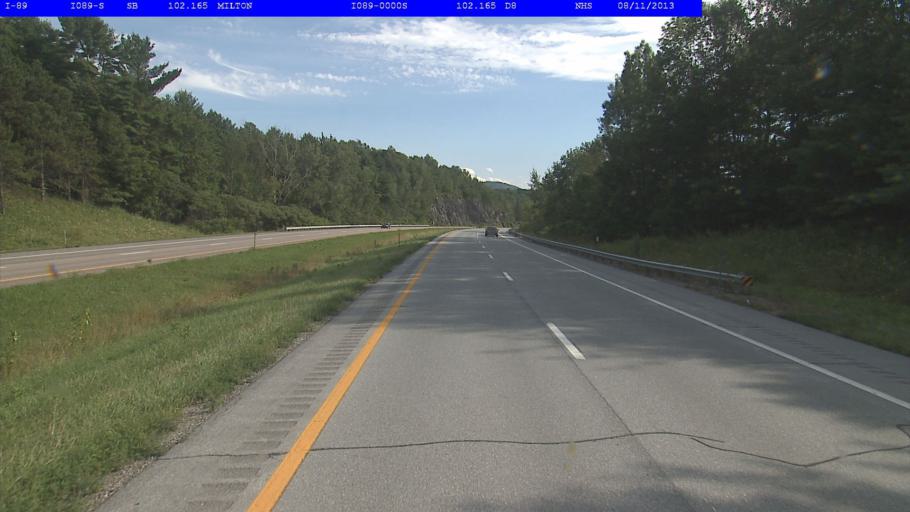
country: US
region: Vermont
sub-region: Chittenden County
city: Milton
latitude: 44.6444
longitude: -73.1398
